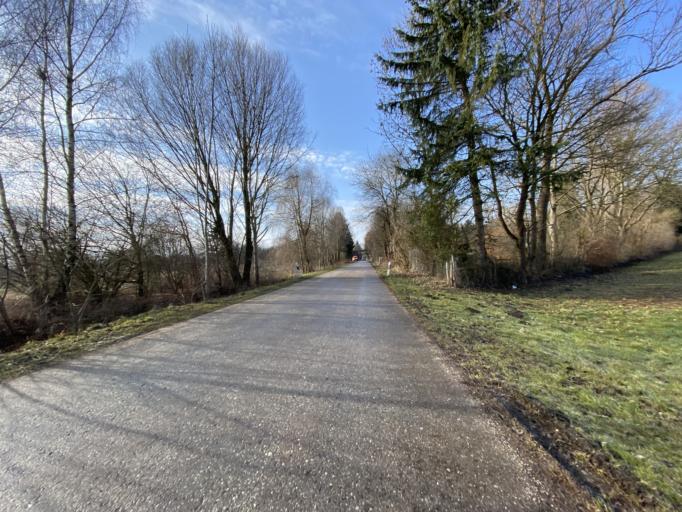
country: DE
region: Bavaria
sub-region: Upper Bavaria
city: Unterfoehring
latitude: 48.1771
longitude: 11.6541
